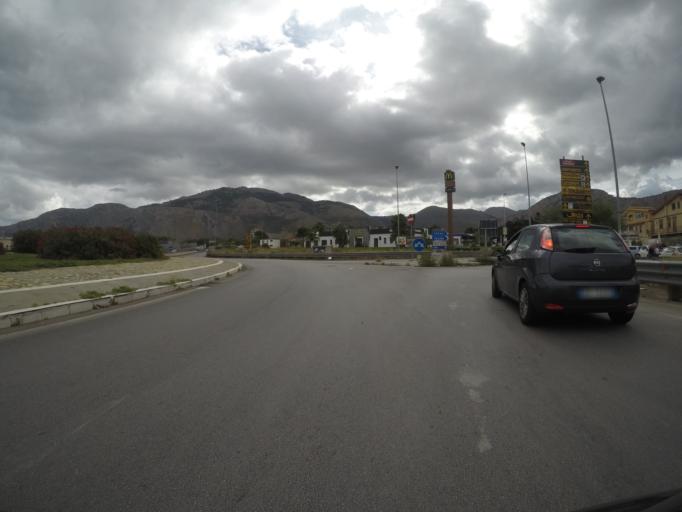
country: IT
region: Sicily
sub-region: Palermo
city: Capaci
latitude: 38.1727
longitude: 13.2153
